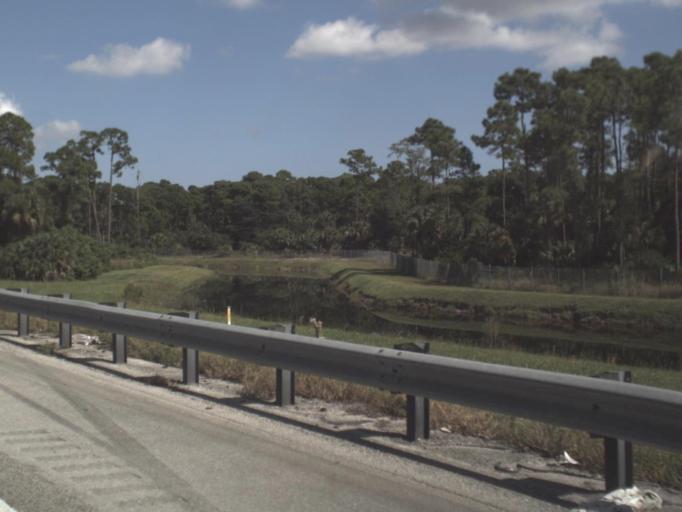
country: US
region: Florida
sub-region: Palm Beach County
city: Palm Beach Gardens
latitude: 26.7724
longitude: -80.1330
